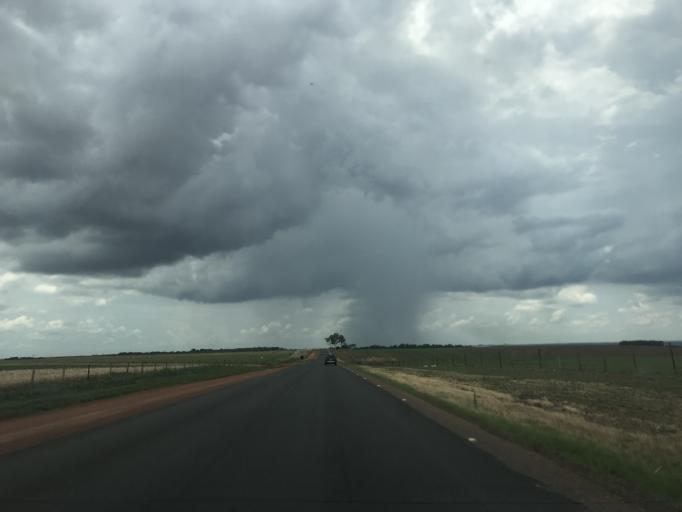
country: BR
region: Goias
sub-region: Vianopolis
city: Vianopolis
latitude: -16.8257
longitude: -48.5282
